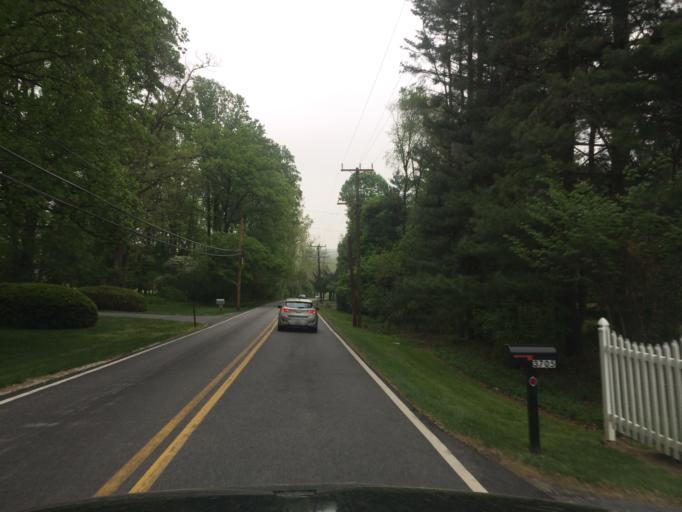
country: US
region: Maryland
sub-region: Howard County
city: Columbia
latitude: 39.2694
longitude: -76.9162
